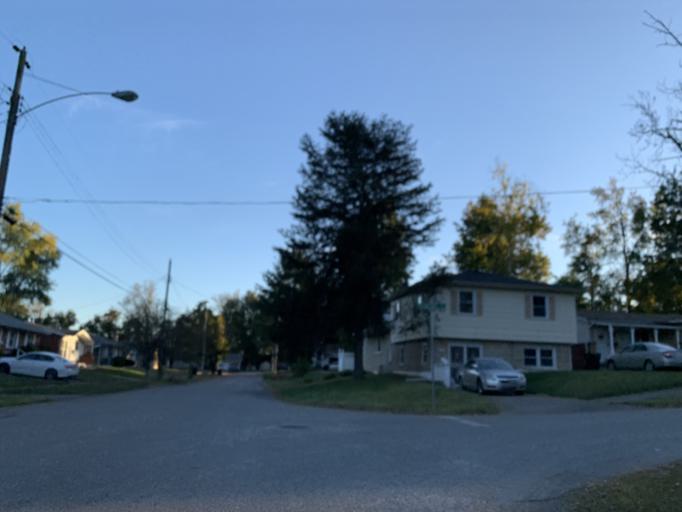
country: US
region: Kentucky
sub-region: Jefferson County
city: Shively
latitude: 38.2397
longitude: -85.8282
